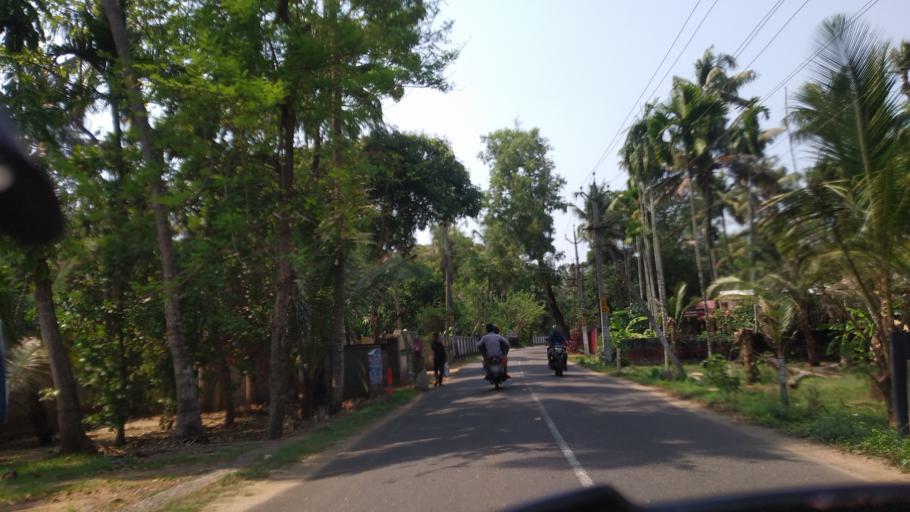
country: IN
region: Kerala
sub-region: Thrissur District
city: Irinjalakuda
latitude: 10.3224
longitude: 76.1242
